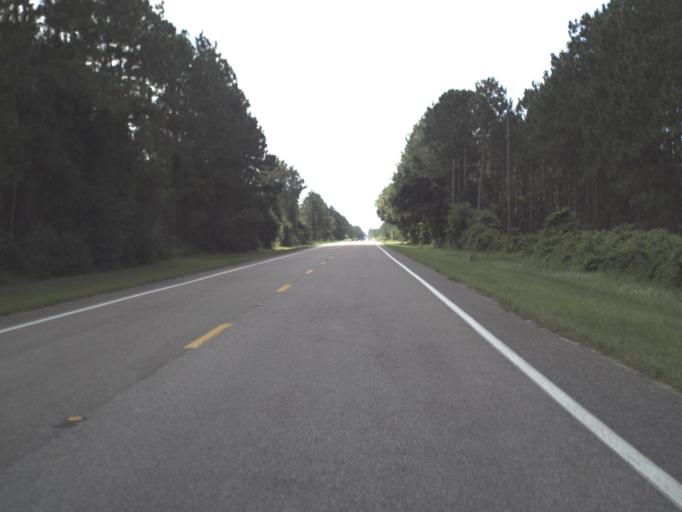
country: US
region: Florida
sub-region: Putnam County
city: East Palatka
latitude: 29.5665
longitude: -81.5459
